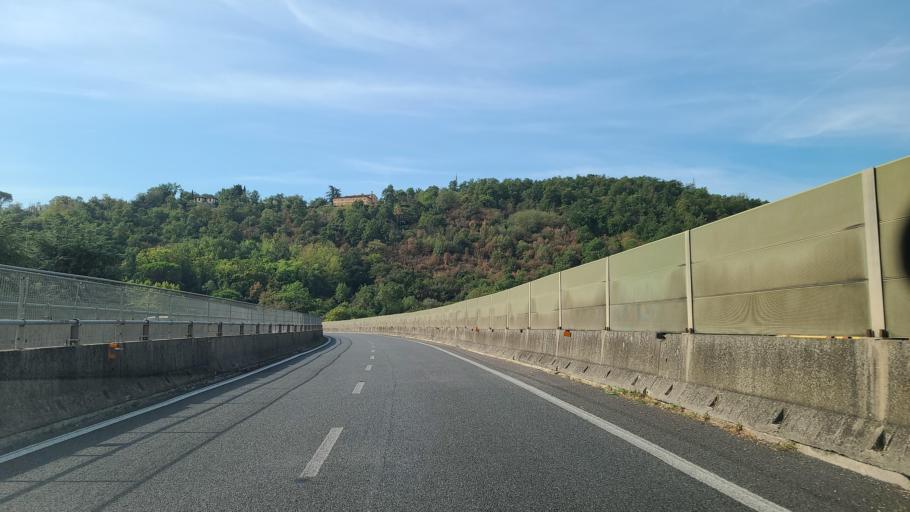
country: IT
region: Tuscany
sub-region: Province of Florence
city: Tavarnuzze
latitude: 43.7095
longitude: 11.2131
